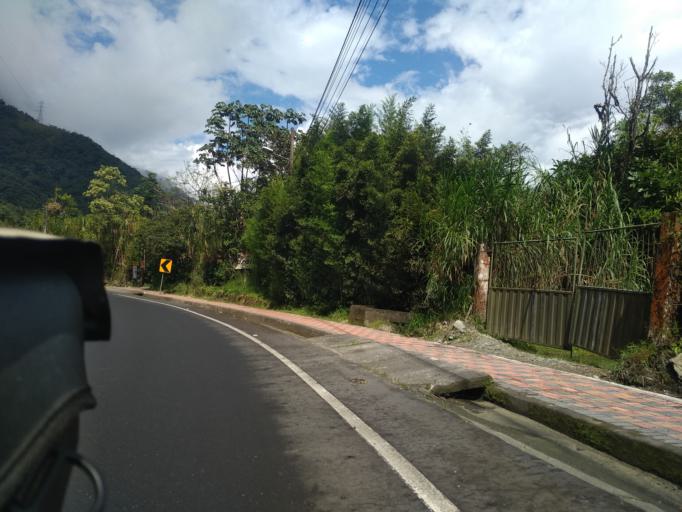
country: EC
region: Tungurahua
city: Banos
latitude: -1.4020
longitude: -78.2880
